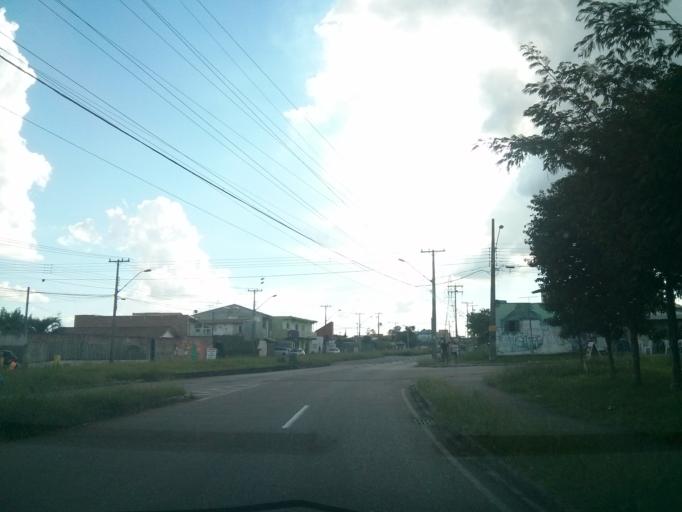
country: BR
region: Parana
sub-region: Sao Jose Dos Pinhais
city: Sao Jose dos Pinhais
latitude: -25.5255
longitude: -49.2323
